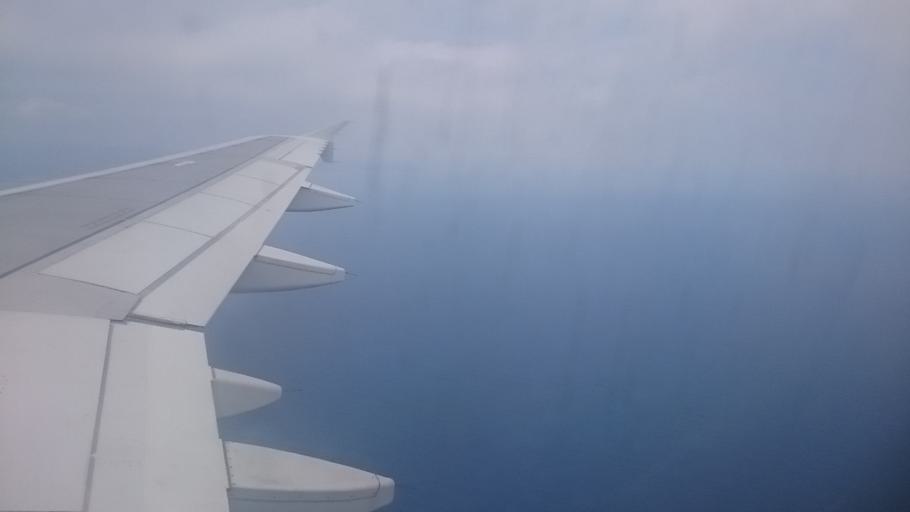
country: ES
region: Catalonia
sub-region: Provincia de Barcelona
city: Caldes d'Estrac
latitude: 41.4472
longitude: 2.5793
